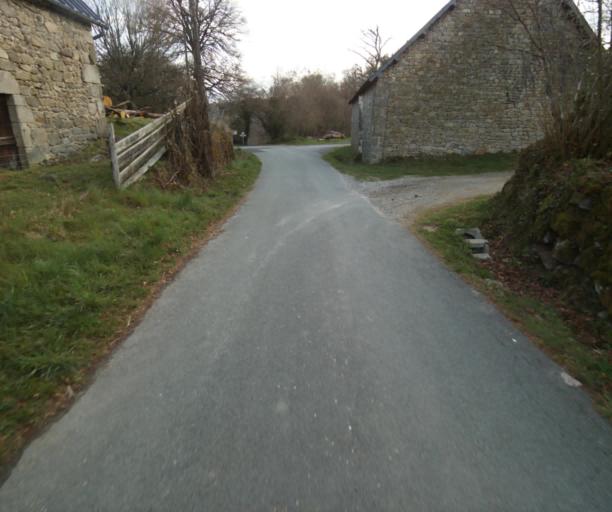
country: FR
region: Limousin
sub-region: Departement de la Correze
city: Correze
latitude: 45.3784
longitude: 1.8849
